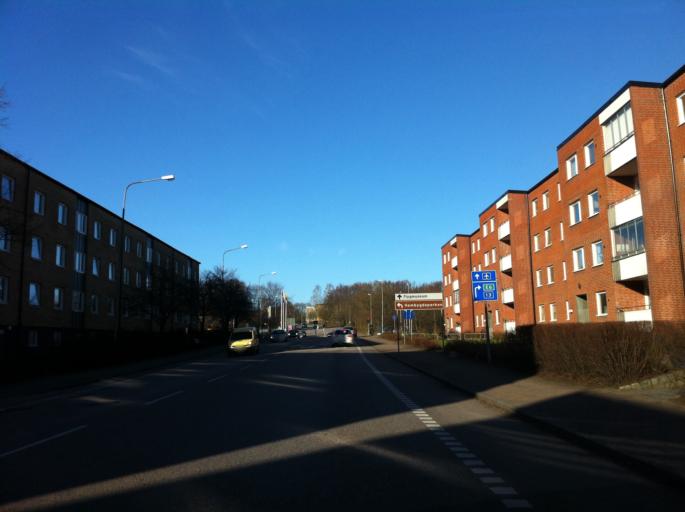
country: SE
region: Skane
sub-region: Angelholms Kommun
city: AEngelholm
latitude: 56.2463
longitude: 12.8730
